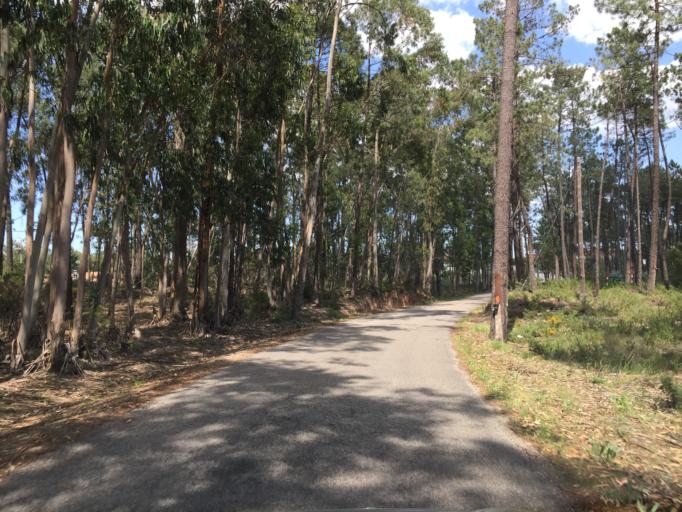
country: PT
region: Santarem
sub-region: Ourem
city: Ourem
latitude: 39.6777
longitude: -8.5707
